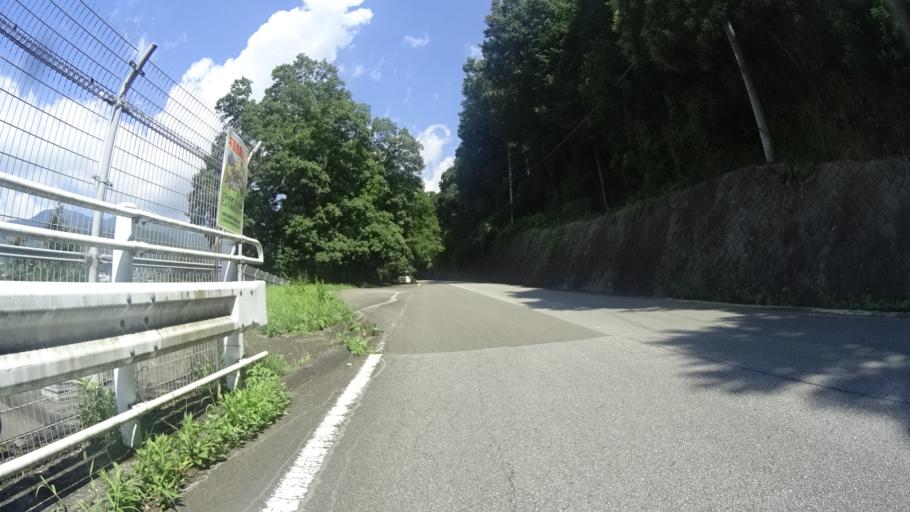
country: JP
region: Yamanashi
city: Enzan
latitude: 35.7548
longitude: 138.7113
